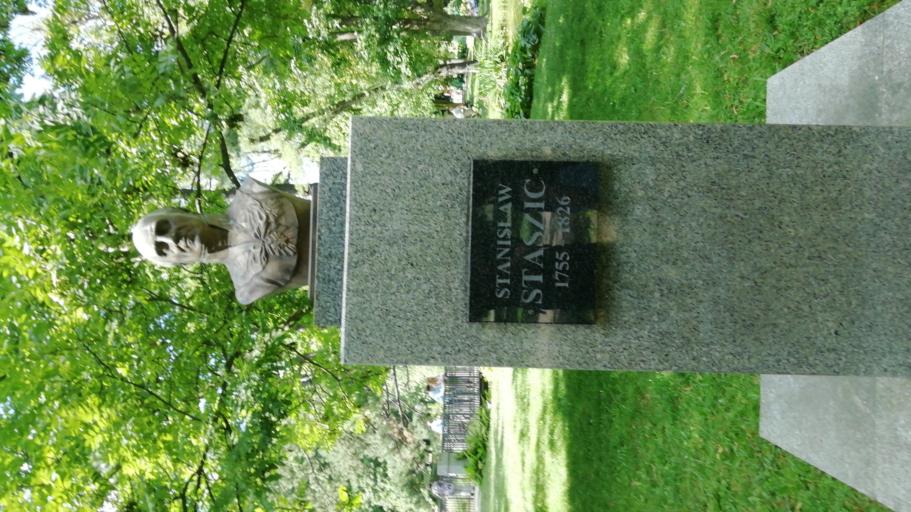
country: PL
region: Silesian Voivodeship
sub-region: Czestochowa
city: Czestochowa
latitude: 50.8116
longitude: 19.1031
